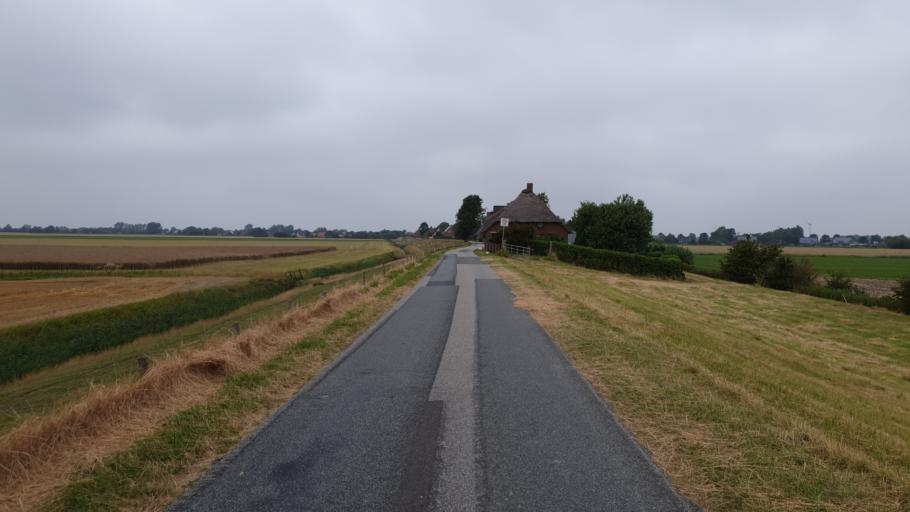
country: DE
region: Schleswig-Holstein
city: Elisabeth-Sophien-Koog
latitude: 54.4814
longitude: 8.8928
